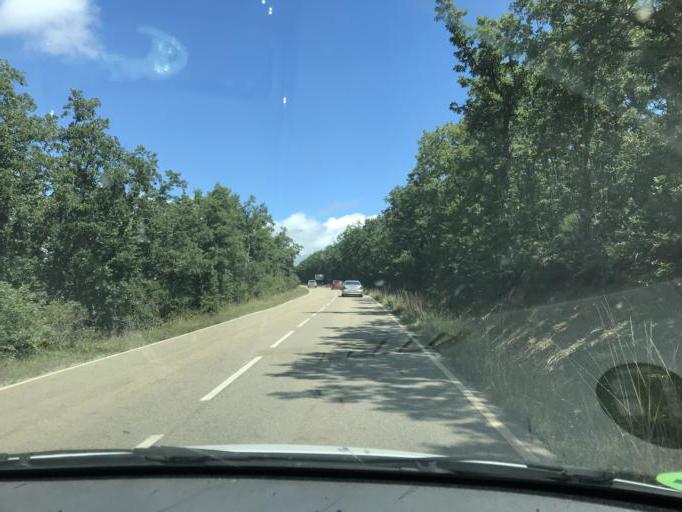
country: ES
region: Castille and Leon
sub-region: Provincia de Palencia
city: Cervera de Pisuerga
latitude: 42.8819
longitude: -4.4932
